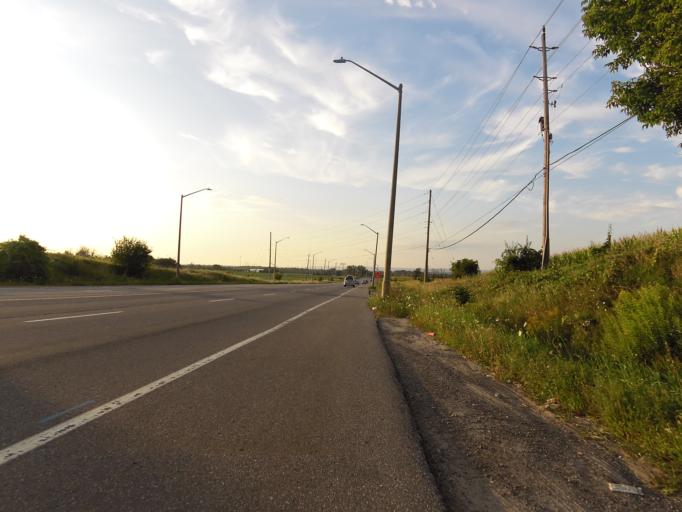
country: CA
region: Ontario
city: Bells Corners
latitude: 45.3294
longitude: -75.8373
